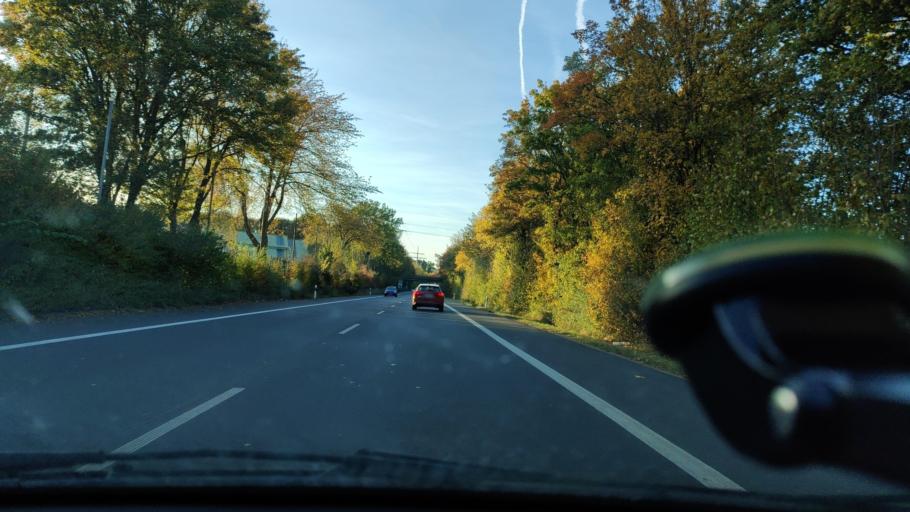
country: DE
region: North Rhine-Westphalia
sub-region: Regierungsbezirk Dusseldorf
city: Monchengladbach
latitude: 51.2282
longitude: 6.4703
